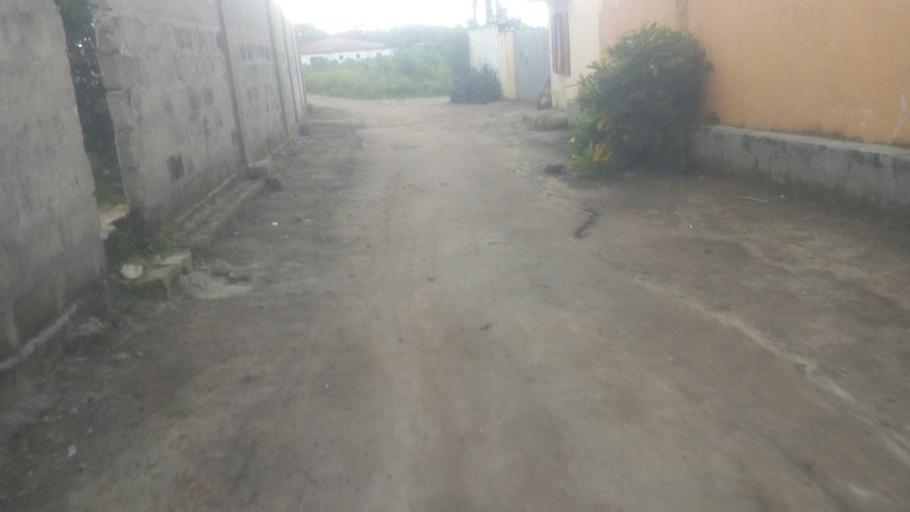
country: SL
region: Northern Province
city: Masoyila
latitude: 8.5781
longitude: -13.1657
